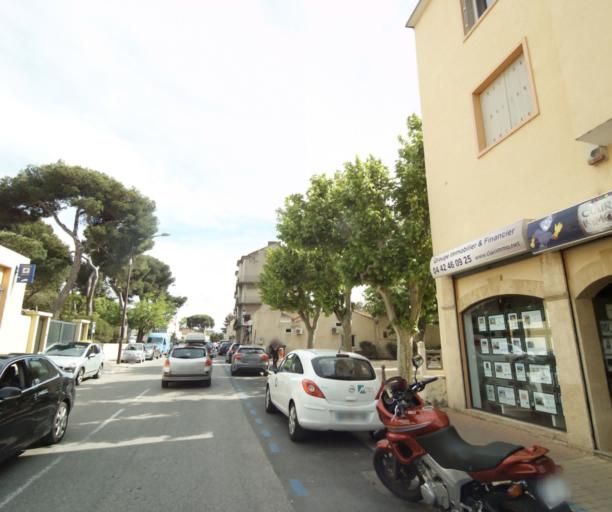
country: FR
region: Provence-Alpes-Cote d'Azur
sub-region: Departement des Bouches-du-Rhone
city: Rognac
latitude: 43.4880
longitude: 5.2300
